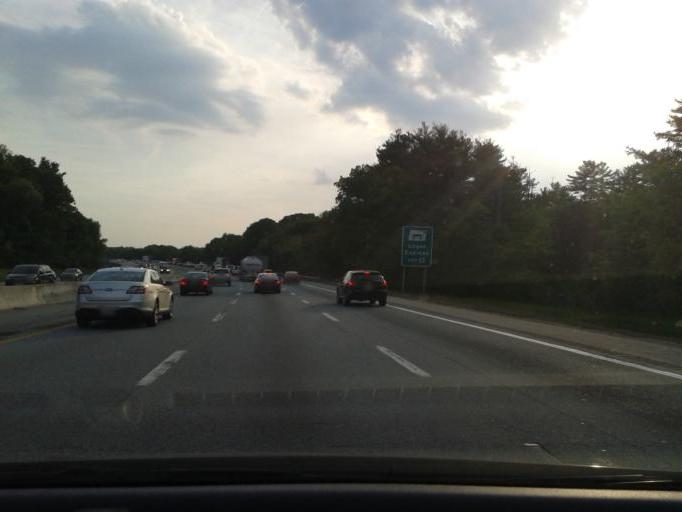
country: US
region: Massachusetts
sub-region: Middlesex County
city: Cochituate
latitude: 42.3170
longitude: -71.3541
